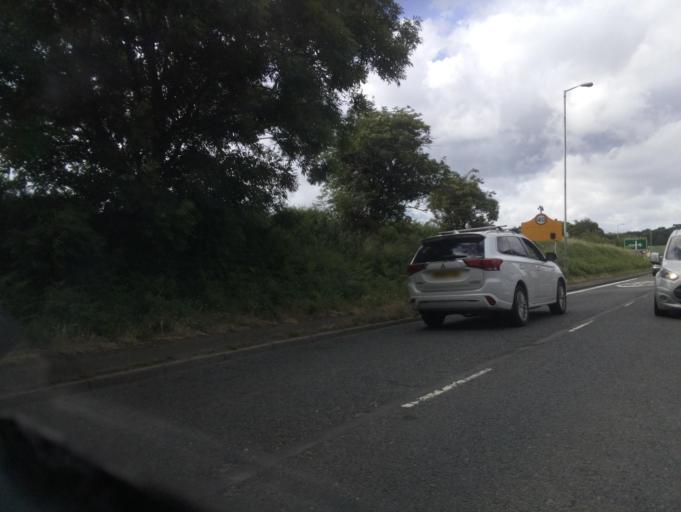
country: GB
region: England
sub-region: Worcestershire
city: Kidderminster
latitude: 52.4038
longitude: -2.2282
